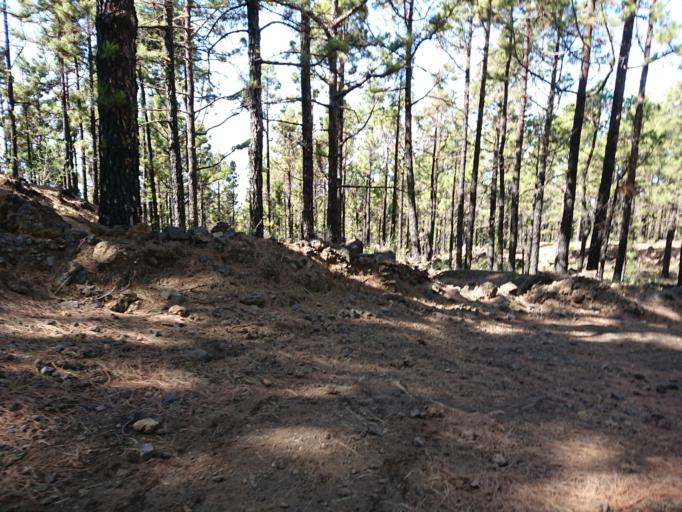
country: ES
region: Canary Islands
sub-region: Provincia de Santa Cruz de Tenerife
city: El Paso
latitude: 28.5928
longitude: -17.8606
